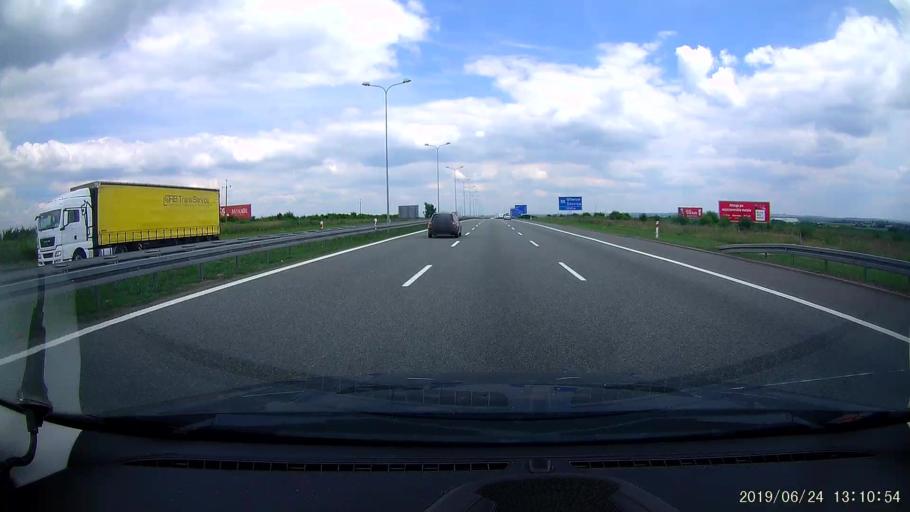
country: PL
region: Silesian Voivodeship
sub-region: Powiat gliwicki
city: Gieraltowice
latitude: 50.2309
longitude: 18.6998
